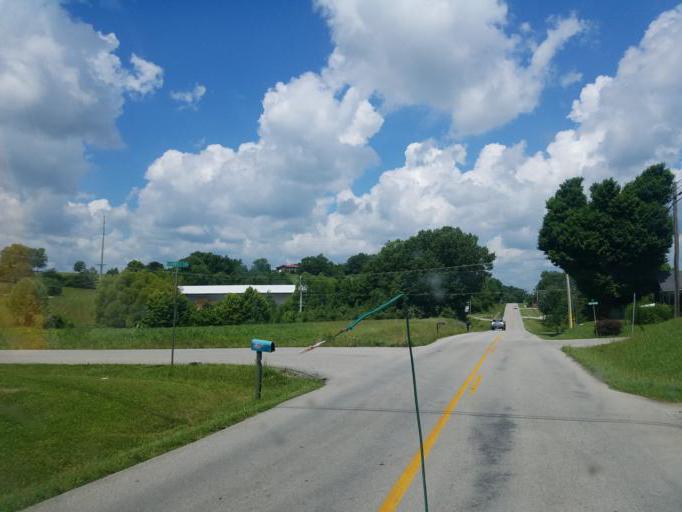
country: US
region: Kentucky
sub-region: Grayson County
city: Leitchfield
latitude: 37.4931
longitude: -86.2995
